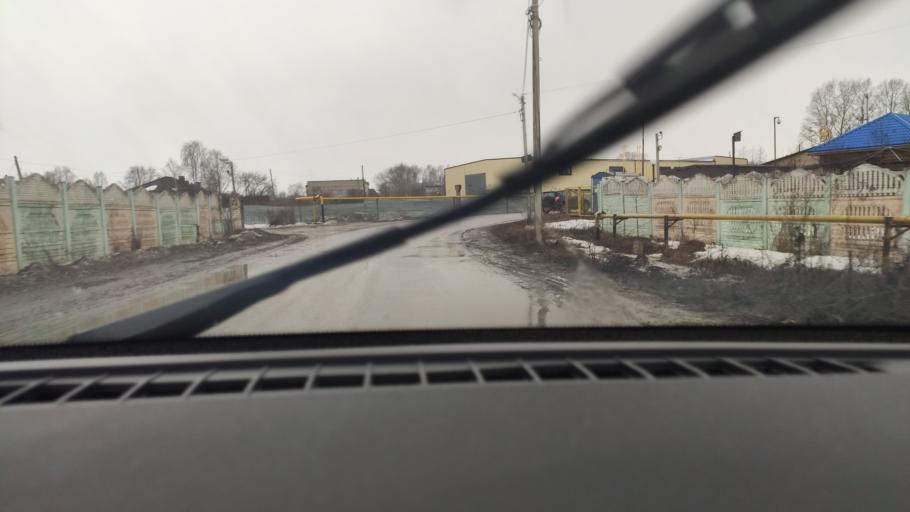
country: RU
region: Perm
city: Kultayevo
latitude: 57.8993
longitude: 55.9458
